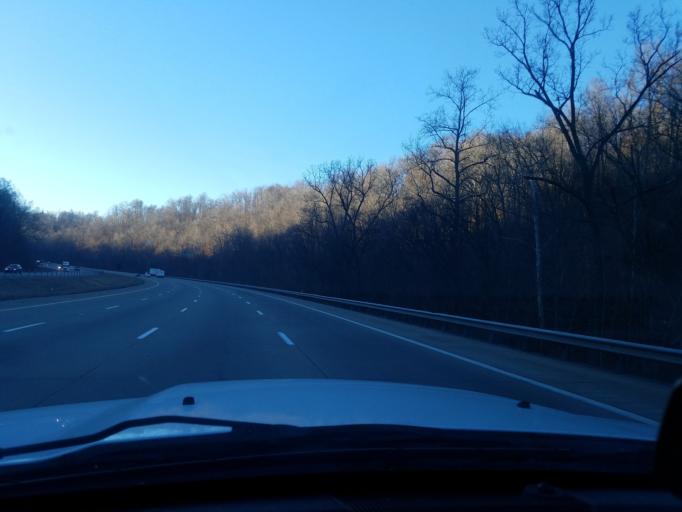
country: US
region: Kentucky
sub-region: Hardin County
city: Elizabethtown
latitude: 37.7599
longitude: -85.7966
